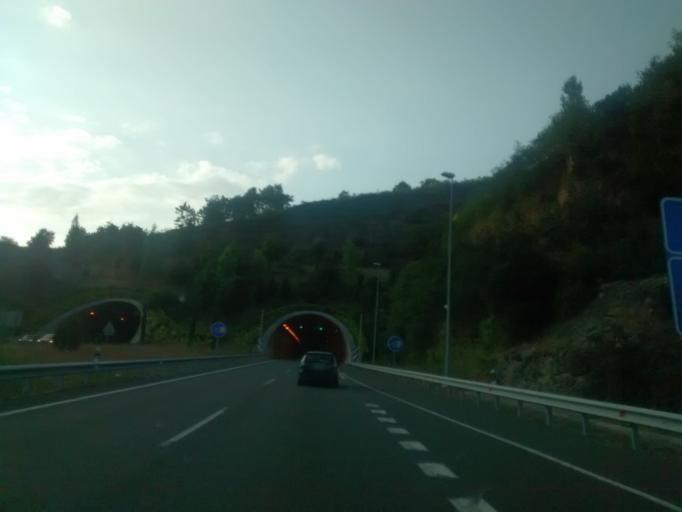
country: ES
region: Cantabria
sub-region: Provincia de Cantabria
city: Arenas de Iguna
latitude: 43.2031
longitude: -4.0728
